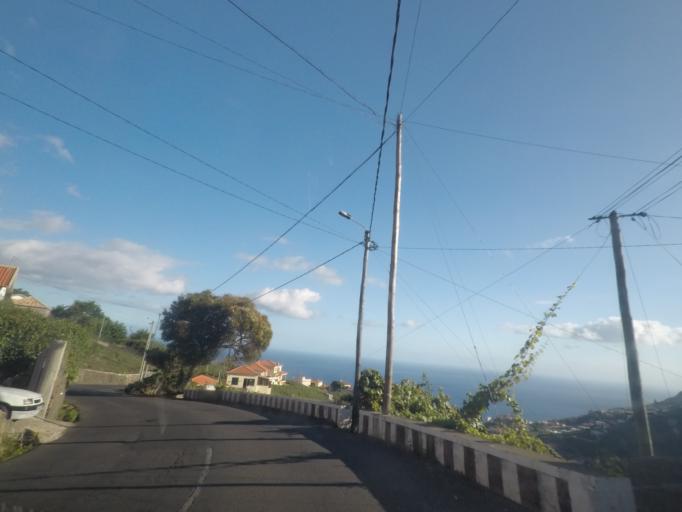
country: PT
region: Madeira
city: Camara de Lobos
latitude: 32.6682
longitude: -16.9802
